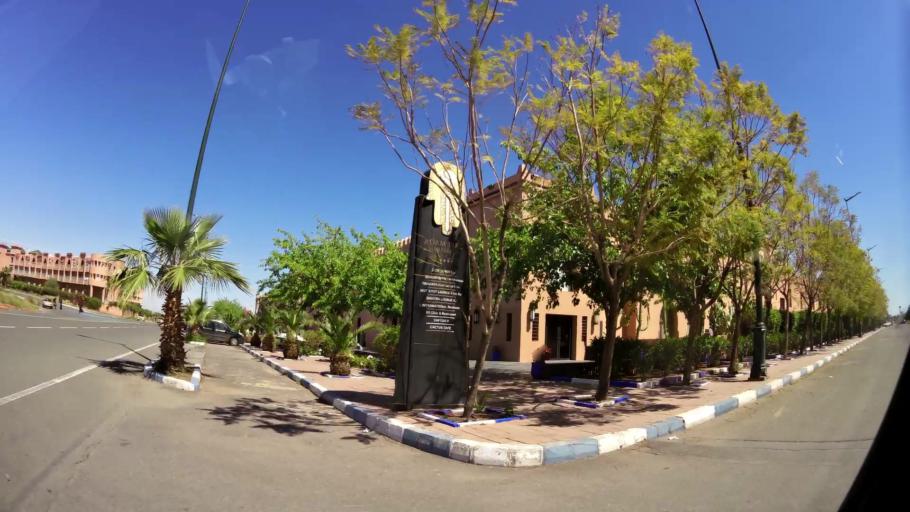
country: MA
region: Marrakech-Tensift-Al Haouz
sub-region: Marrakech
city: Marrakesh
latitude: 31.5957
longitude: -7.9897
